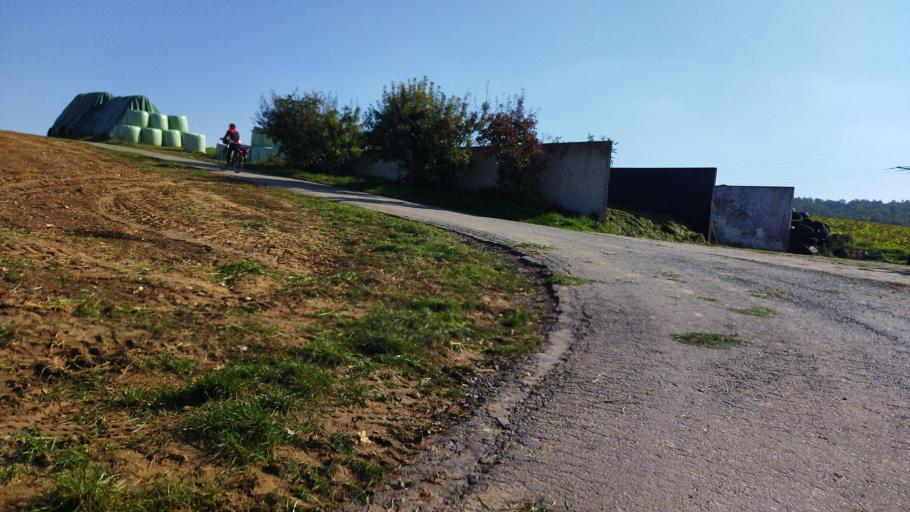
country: DE
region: Baden-Wuerttemberg
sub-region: Regierungsbezirk Stuttgart
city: Ilsfeld
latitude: 49.0465
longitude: 9.2485
